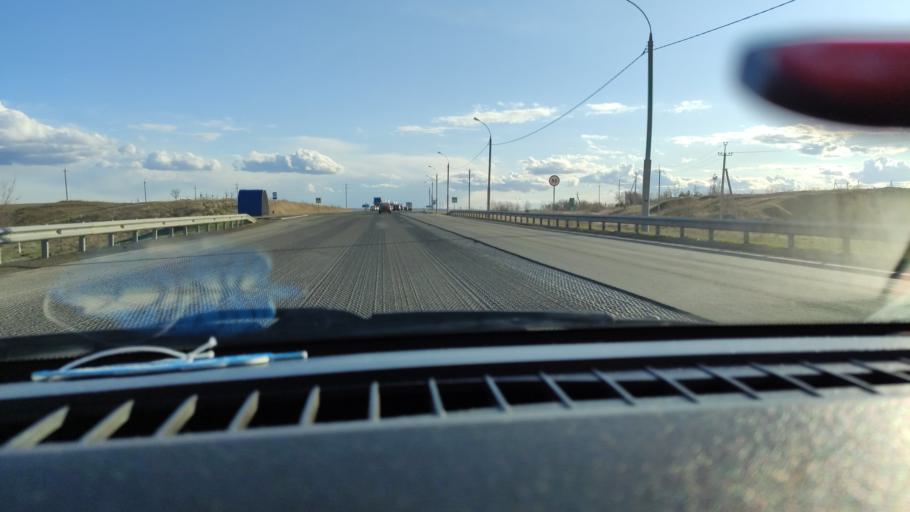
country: RU
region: Saratov
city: Yelshanka
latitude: 51.8157
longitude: 46.2099
